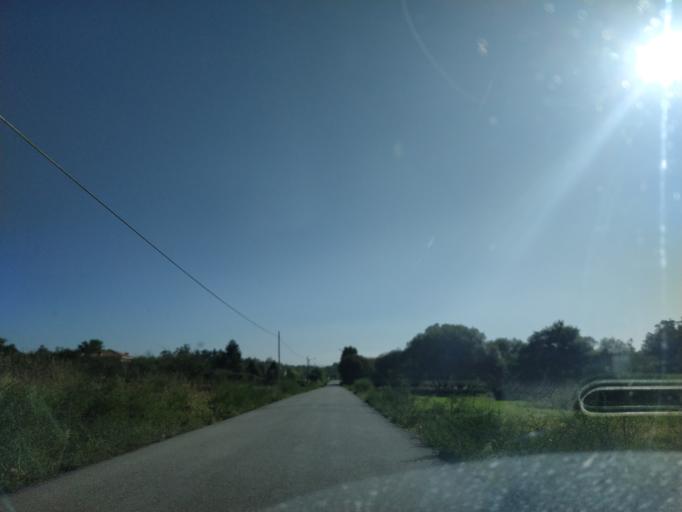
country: ES
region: Galicia
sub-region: Provincia da Coruna
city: Santa Comba
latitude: 43.0020
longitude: -8.7482
